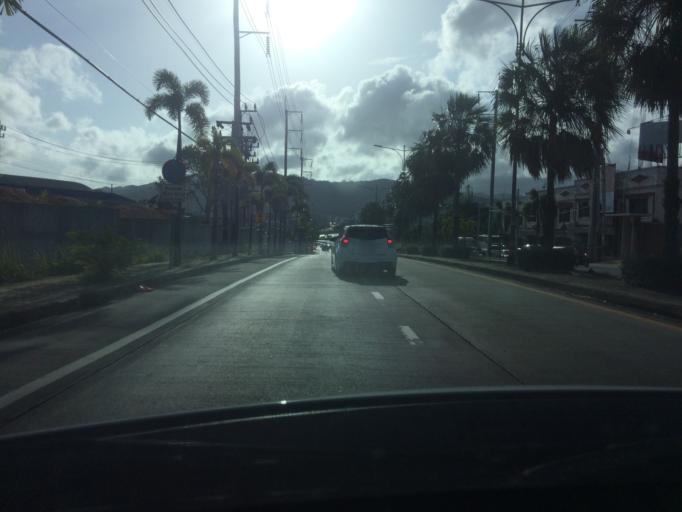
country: TH
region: Phuket
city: Mueang Phuket
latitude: 7.8690
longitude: 98.3768
